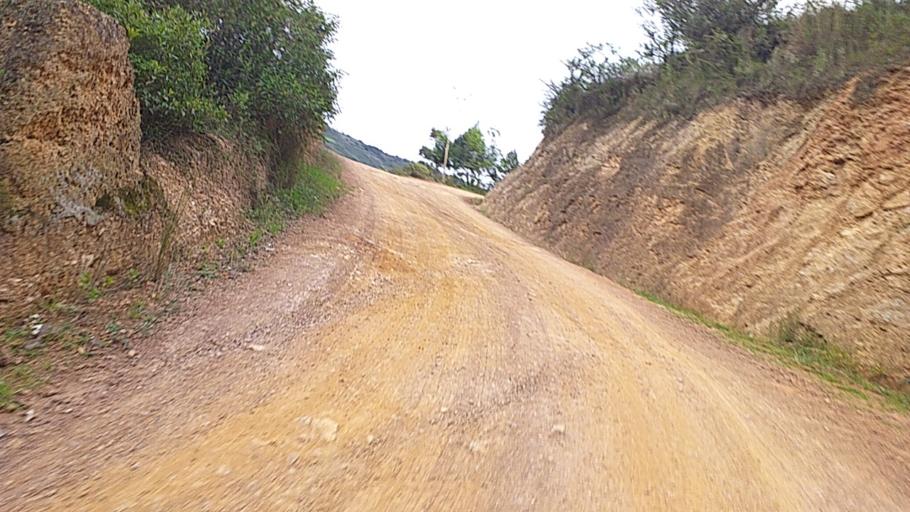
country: CO
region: Boyaca
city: Floresta
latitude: 5.8732
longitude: -72.9188
